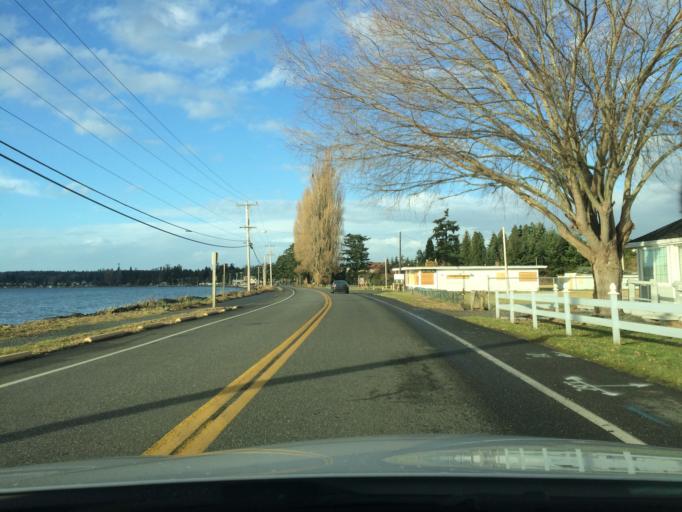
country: US
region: Washington
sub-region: Whatcom County
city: Birch Bay
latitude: 48.9290
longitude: -122.7455
